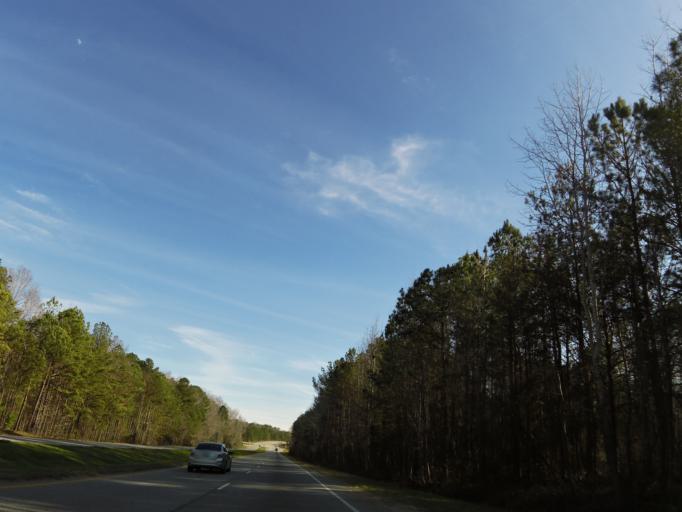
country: US
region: Georgia
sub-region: Chattahoochee County
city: Cusseta
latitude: 32.3118
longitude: -84.7971
